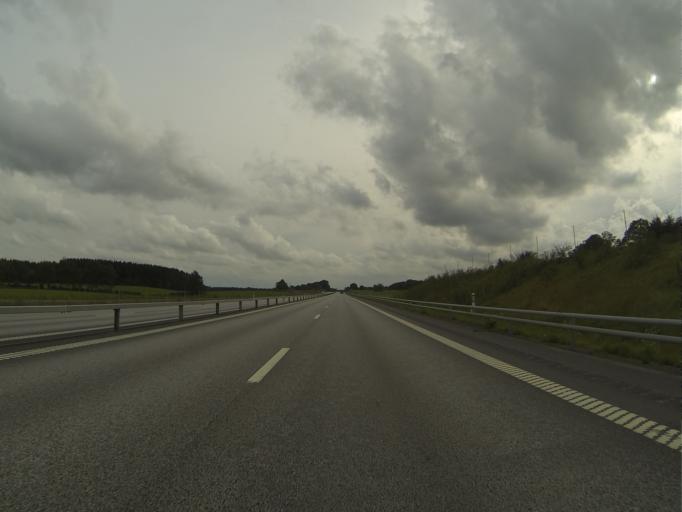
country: SE
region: Skane
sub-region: Horby Kommun
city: Hoerby
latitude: 55.8951
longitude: 13.7225
